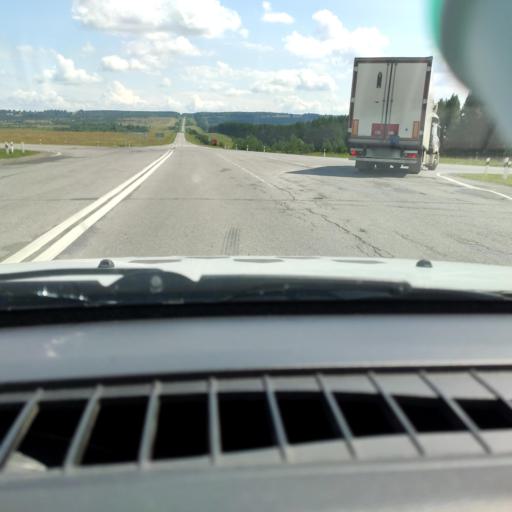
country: RU
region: Chelyabinsk
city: Mezhevoy
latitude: 55.3102
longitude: 58.7328
